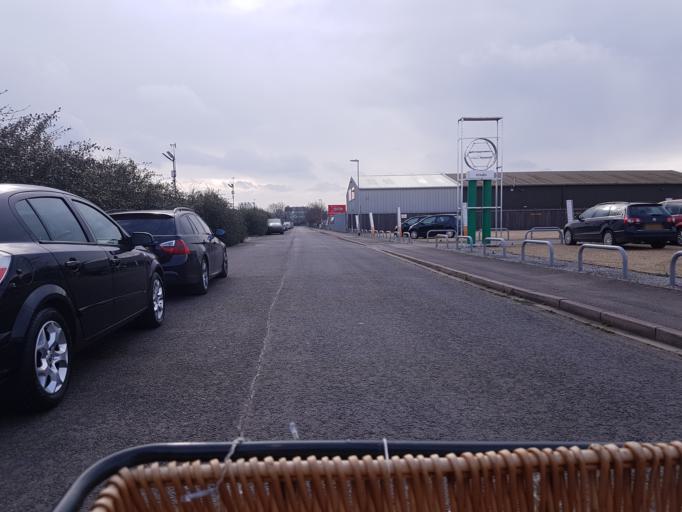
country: GB
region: England
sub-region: Cambridgeshire
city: Waterbeach
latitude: 52.2304
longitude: 0.1588
